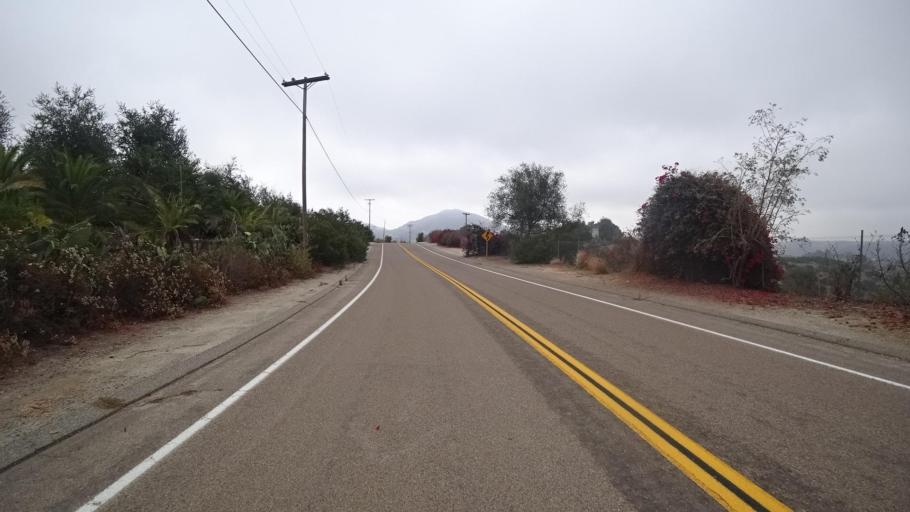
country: US
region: California
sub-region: San Diego County
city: Rainbow
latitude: 33.3844
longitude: -117.1712
